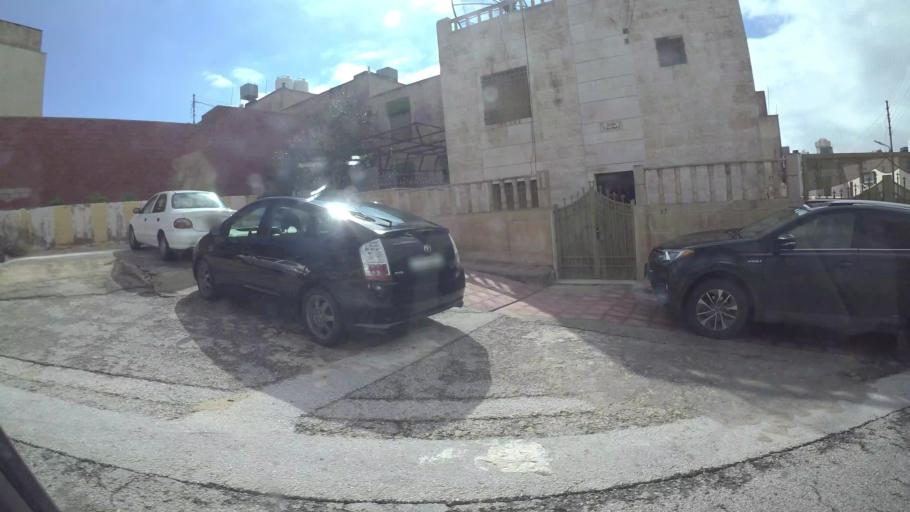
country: JO
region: Amman
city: Al Jubayhah
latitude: 32.0549
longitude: 35.8764
